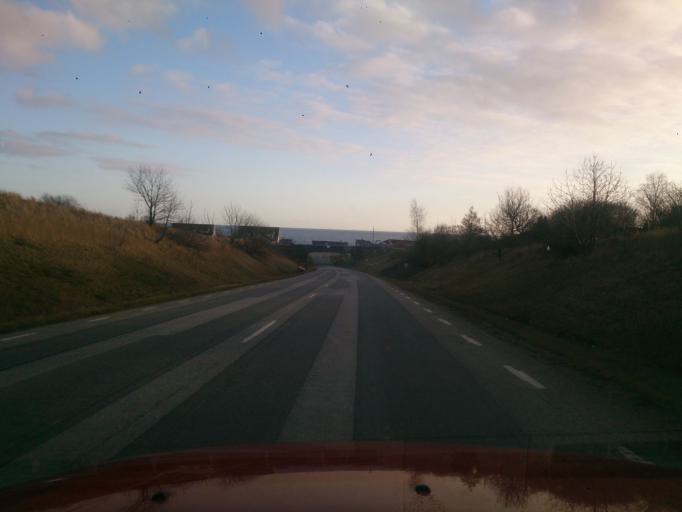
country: SE
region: Skane
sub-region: Ystads Kommun
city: Ystad
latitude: 55.4307
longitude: 13.7186
